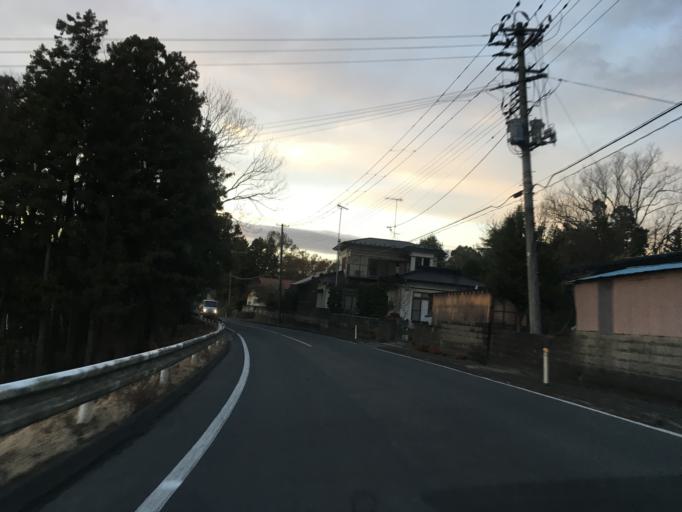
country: JP
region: Iwate
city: Ichinoseki
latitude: 38.7630
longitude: 141.2549
